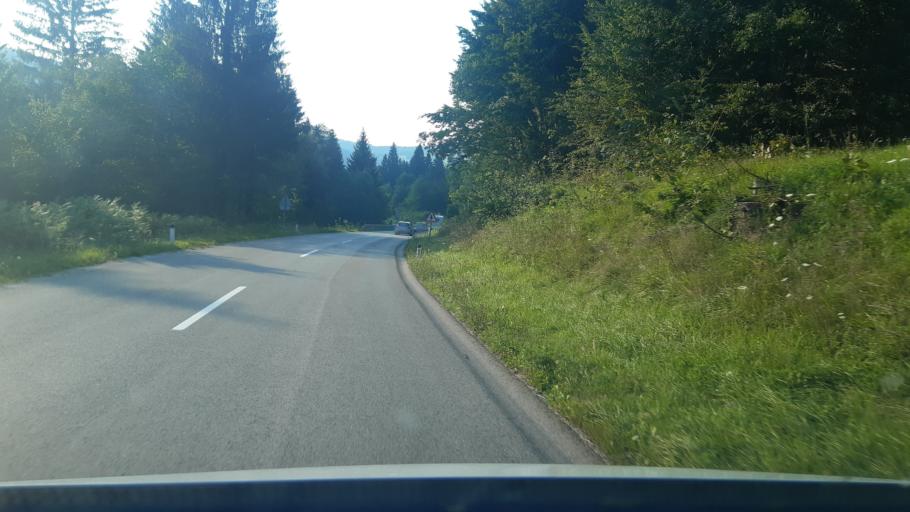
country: SI
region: Semic
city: Semic
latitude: 45.6621
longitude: 15.1130
